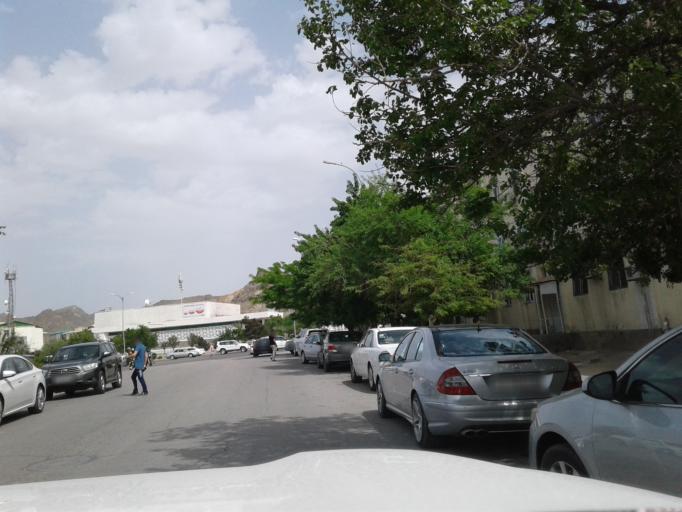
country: TM
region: Balkan
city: Turkmenbasy
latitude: 39.9986
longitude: 52.9698
